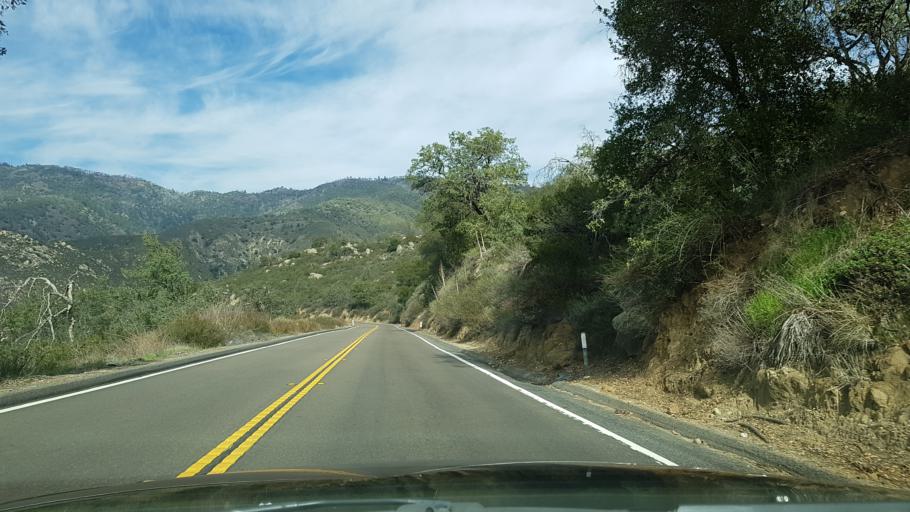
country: US
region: California
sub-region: San Diego County
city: Valley Center
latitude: 33.2976
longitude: -116.9170
